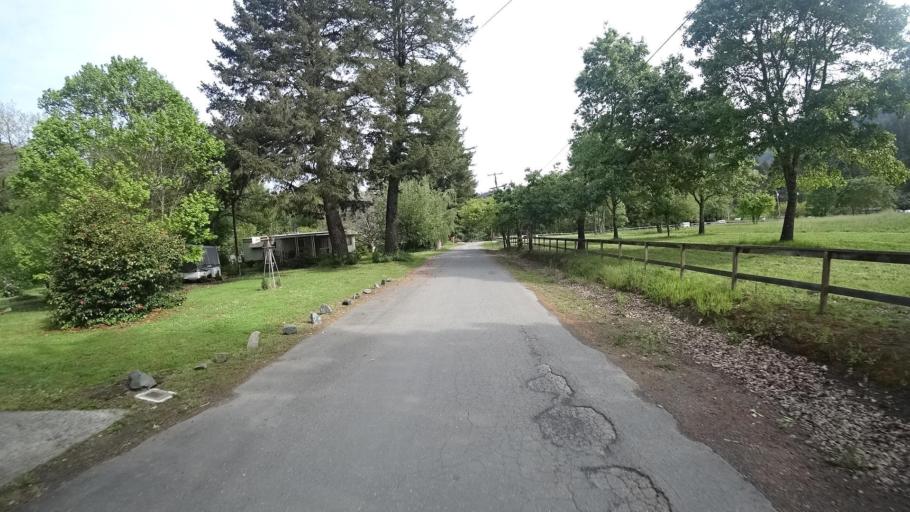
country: US
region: California
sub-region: Humboldt County
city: Redway
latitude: 40.2106
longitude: -123.7899
